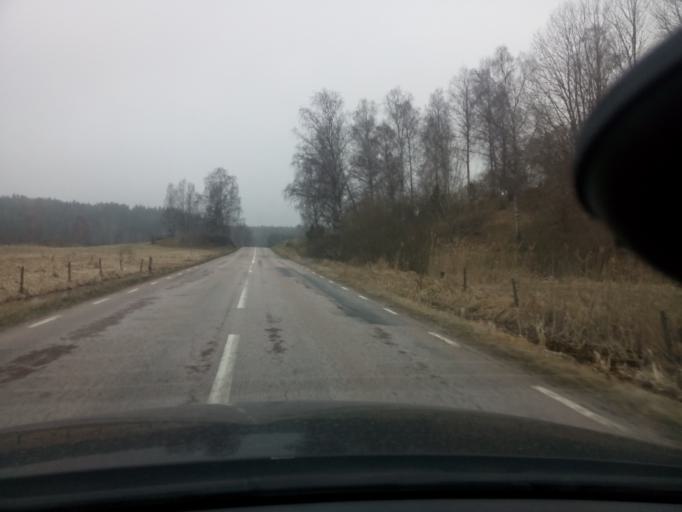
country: SE
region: Soedermanland
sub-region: Gnesta Kommun
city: Gnesta
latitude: 58.9451
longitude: 17.1200
